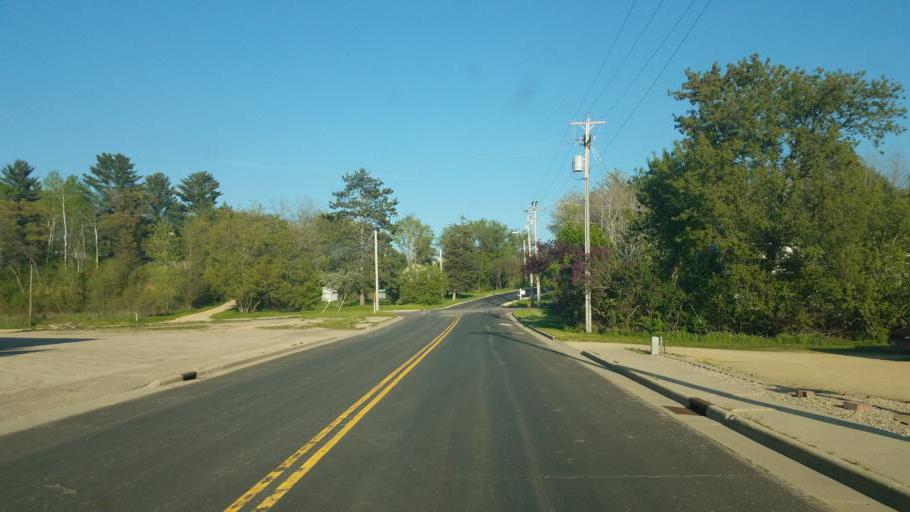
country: US
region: Wisconsin
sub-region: Vernon County
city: Hillsboro
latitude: 43.6521
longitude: -90.3338
